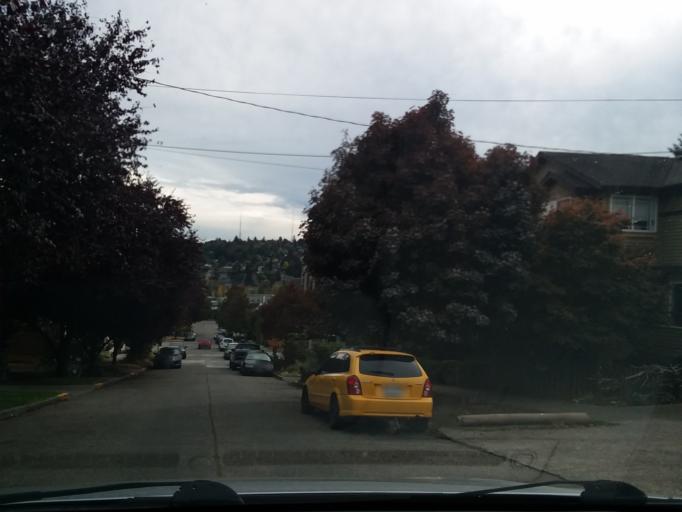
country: US
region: Washington
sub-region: King County
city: Seattle
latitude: 47.6536
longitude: -122.3524
